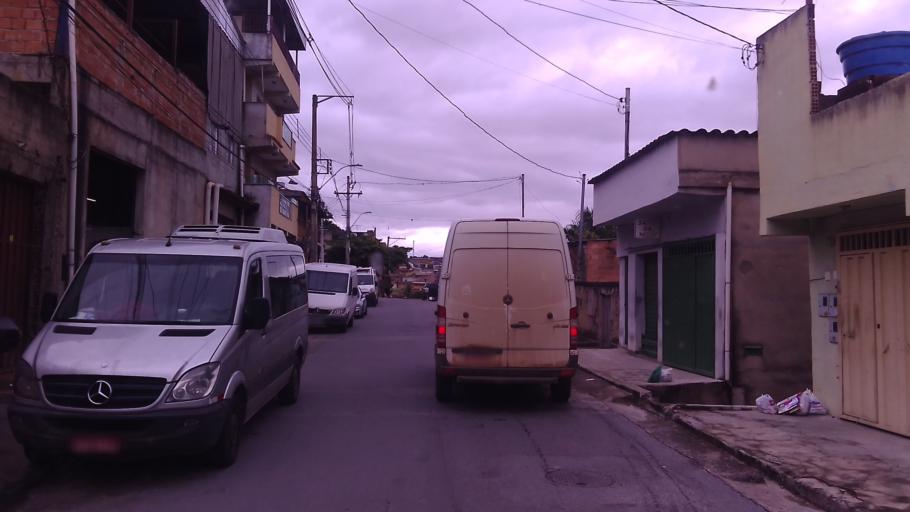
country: BR
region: Minas Gerais
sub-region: Santa Luzia
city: Santa Luzia
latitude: -19.8380
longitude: -43.9047
